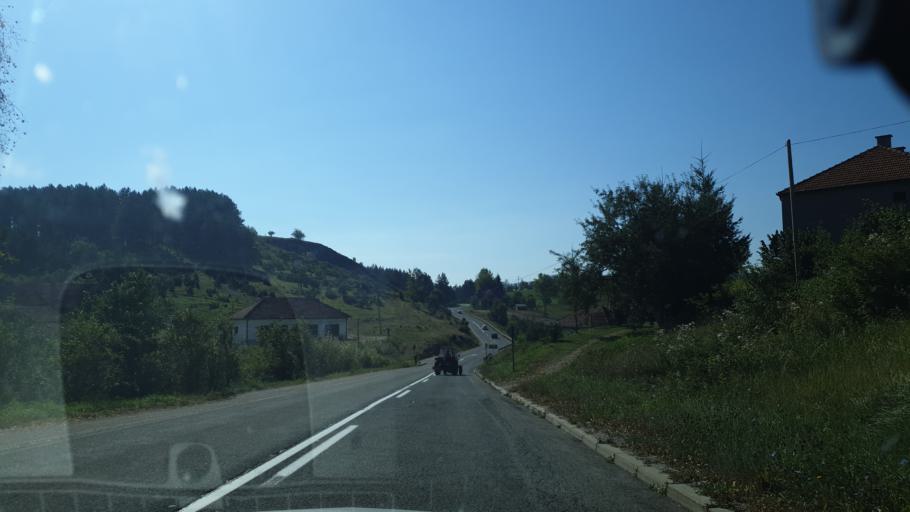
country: RS
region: Central Serbia
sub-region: Zlatiborski Okrug
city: Nova Varos
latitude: 43.5446
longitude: 19.7866
